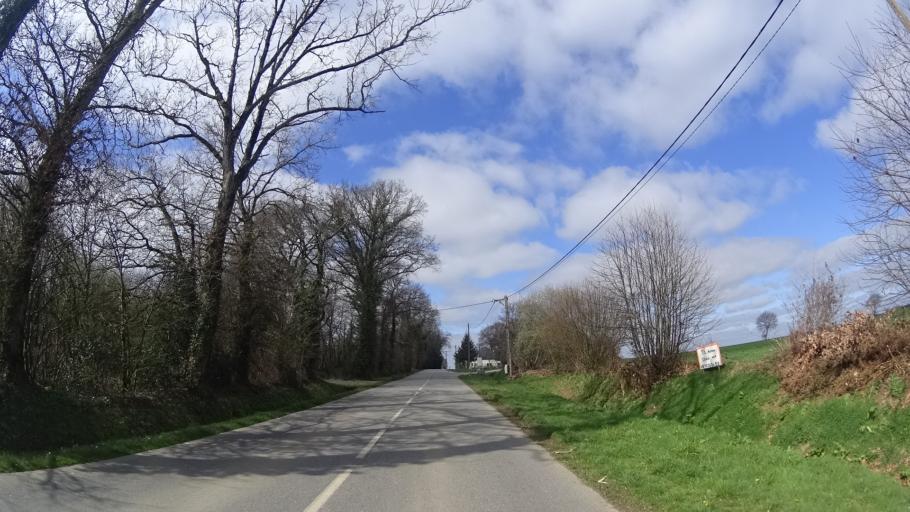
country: FR
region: Brittany
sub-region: Departement du Morbihan
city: Ruffiac
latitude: 47.8230
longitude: -2.2882
